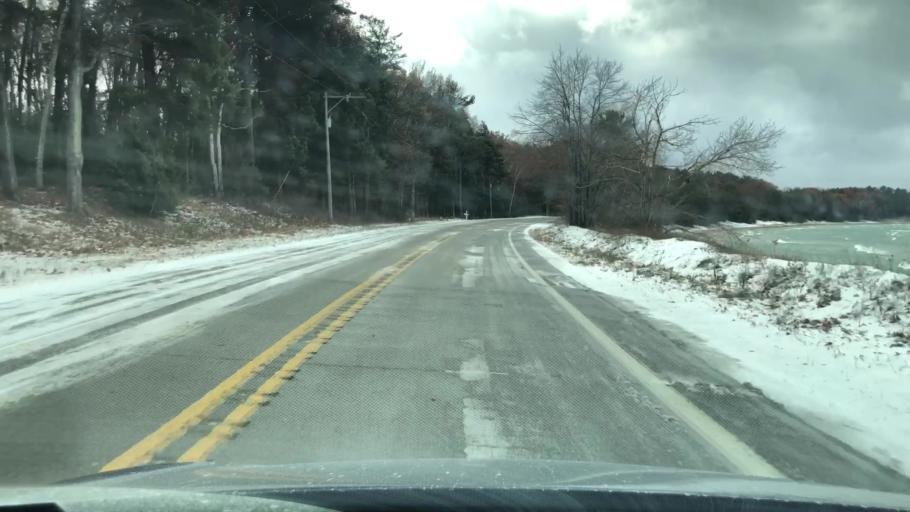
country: US
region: Michigan
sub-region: Antrim County
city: Elk Rapids
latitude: 44.9839
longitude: -85.4958
